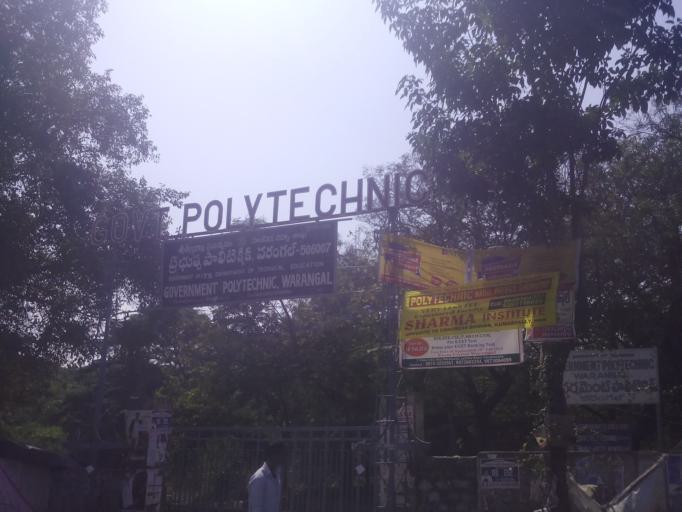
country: IN
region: Telangana
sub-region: Warangal
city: Warangal
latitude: 17.9937
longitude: 79.5914
